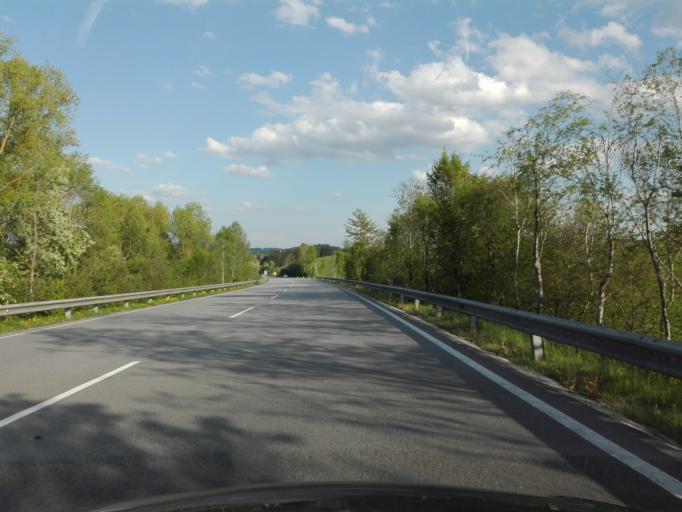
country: AT
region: Upper Austria
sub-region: Politischer Bezirk Rohrbach
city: Kleinzell im Muehlkreis
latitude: 48.4832
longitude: 13.9831
